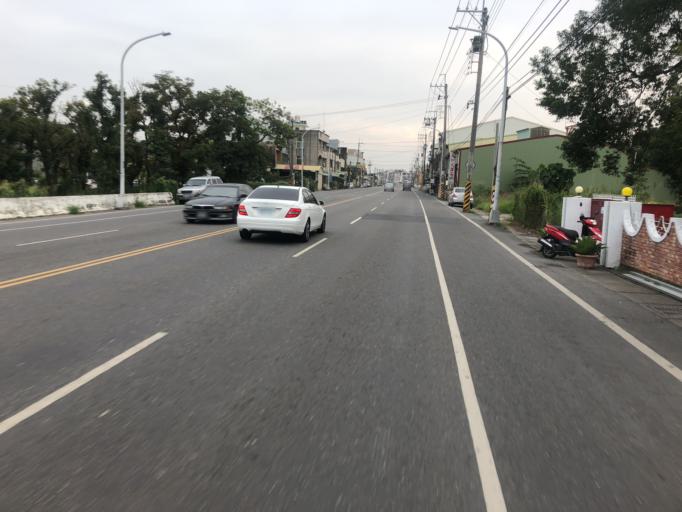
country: TW
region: Taiwan
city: Xinying
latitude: 23.1432
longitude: 120.2881
